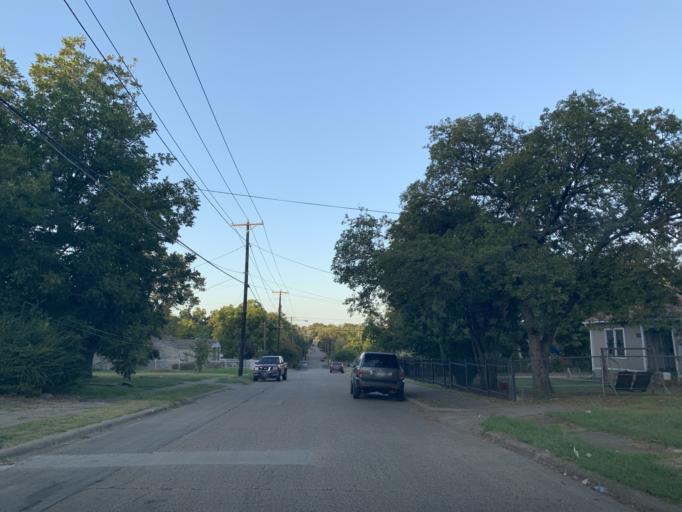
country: US
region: Texas
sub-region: Dallas County
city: Dallas
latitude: 32.7015
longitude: -96.8032
